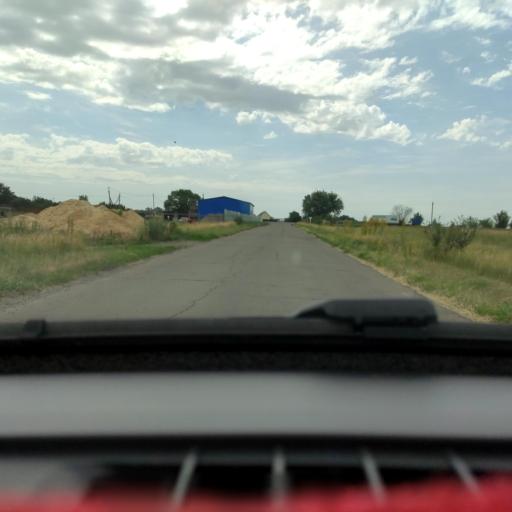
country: RU
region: Voronezj
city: Davydovka
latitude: 51.1939
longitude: 39.4937
